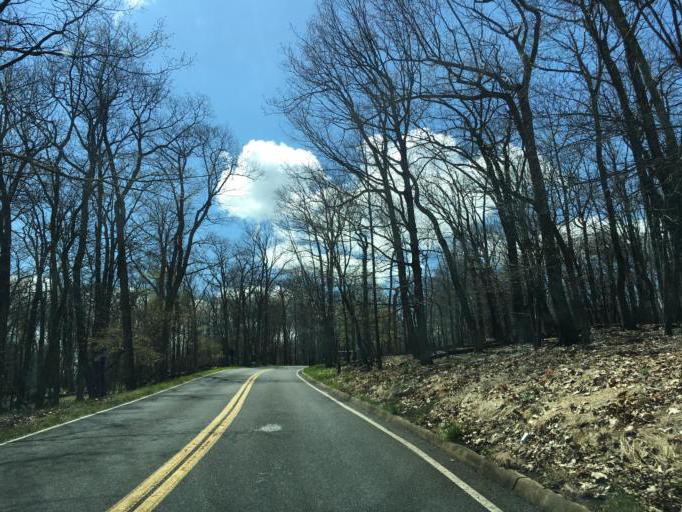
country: US
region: Maryland
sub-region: Frederick County
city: Thurmont
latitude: 39.6423
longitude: -77.4662
